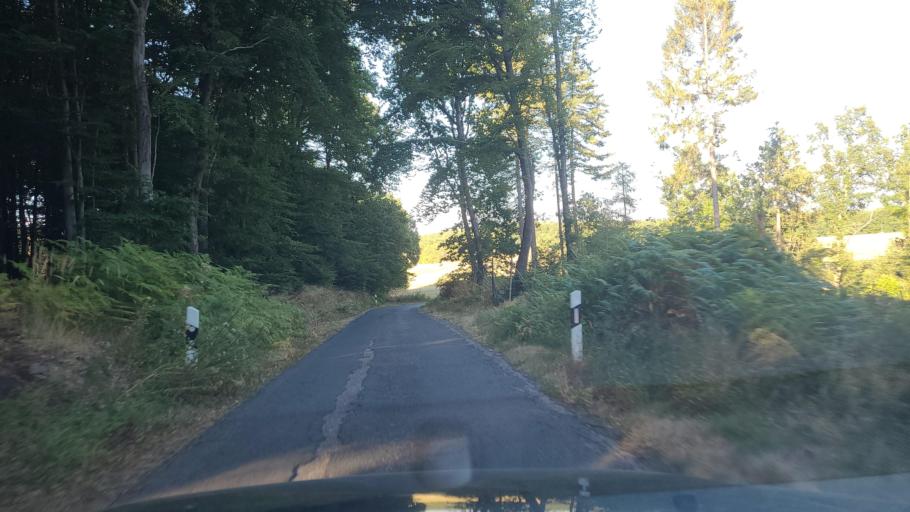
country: DE
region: Rheinland-Pfalz
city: Dierscheid
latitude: 49.8896
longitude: 6.7443
